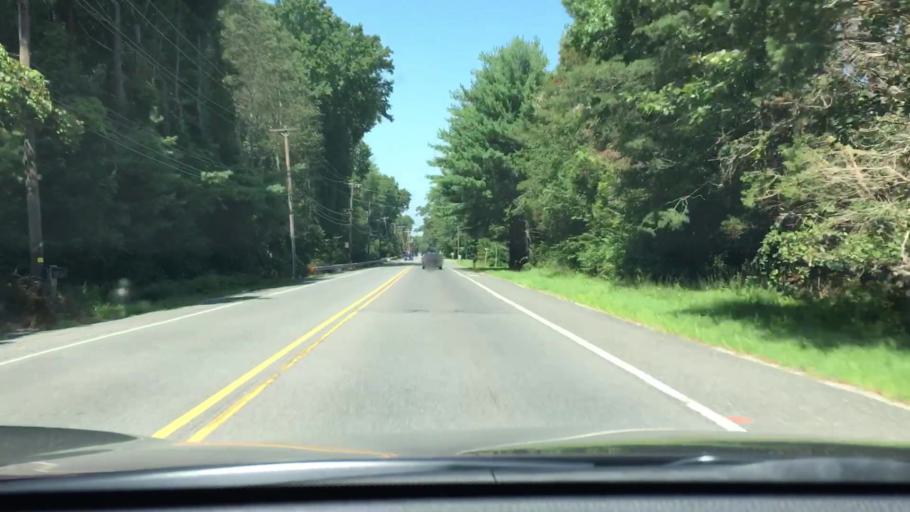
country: US
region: New Jersey
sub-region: Cumberland County
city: Laurel Lake
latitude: 39.3362
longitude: -75.0239
